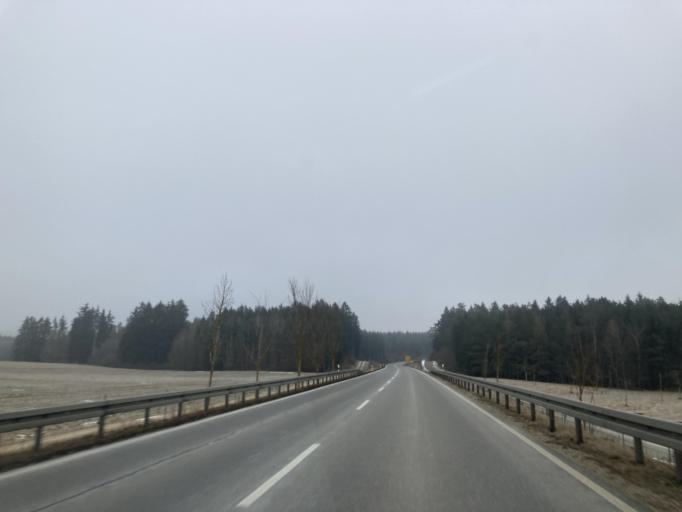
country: DE
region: Baden-Wuerttemberg
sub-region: Freiburg Region
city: Neuhausen ob Eck
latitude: 47.9715
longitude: 8.9511
